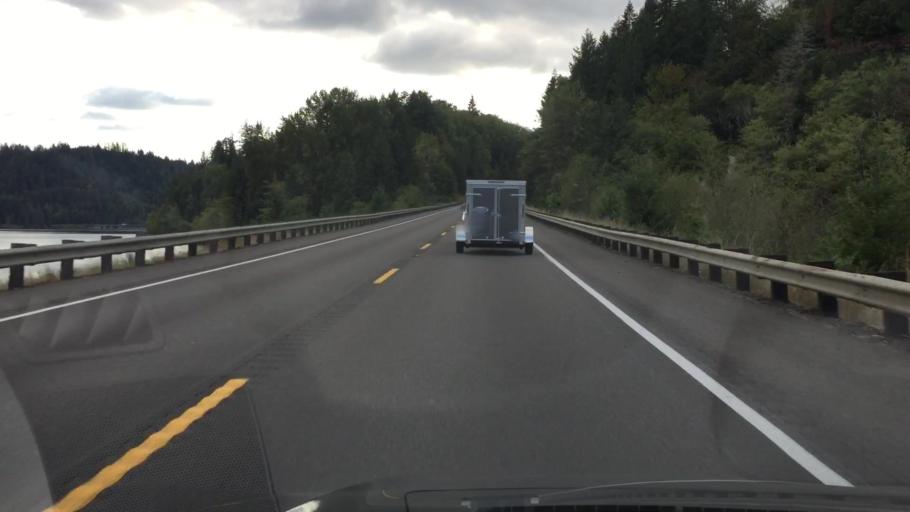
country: US
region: Washington
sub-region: Lewis County
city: Morton
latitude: 46.5146
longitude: -122.5709
